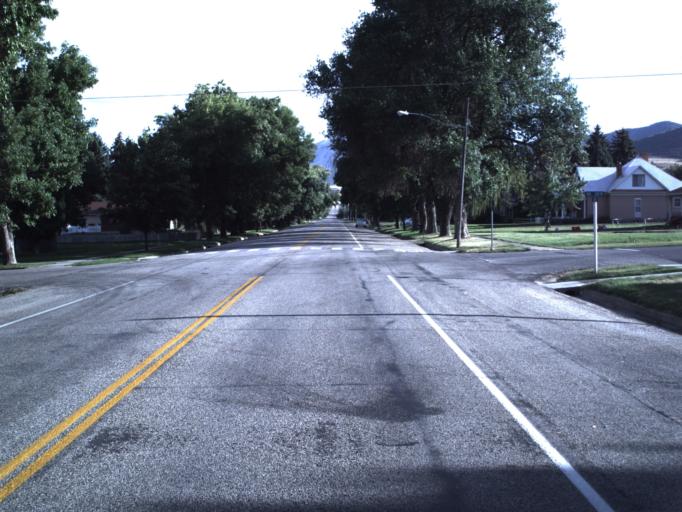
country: US
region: Utah
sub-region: Cache County
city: Wellsville
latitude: 41.6370
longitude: -111.9345
